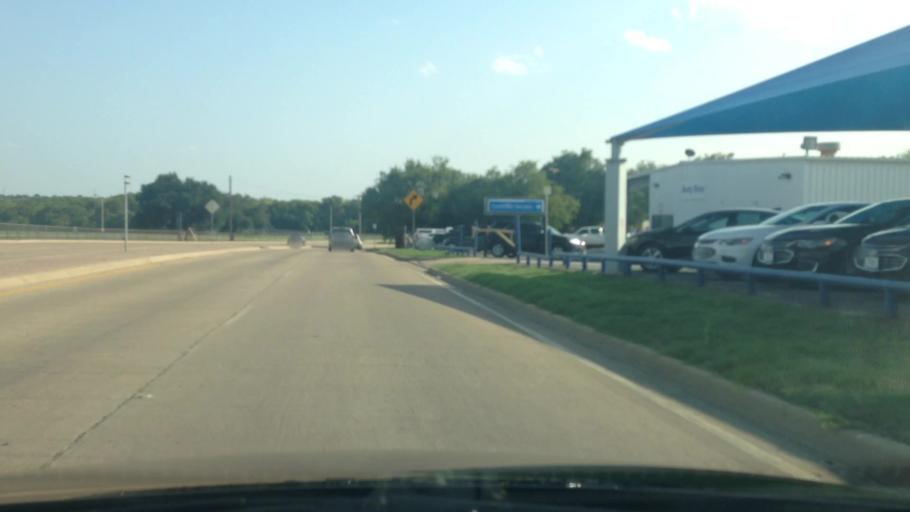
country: US
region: Texas
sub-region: Tarrant County
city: Edgecliff Village
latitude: 32.6638
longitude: -97.3319
